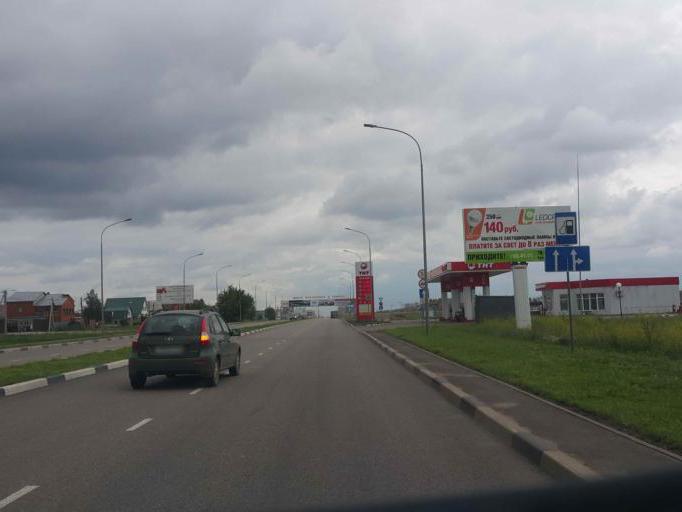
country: RU
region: Tambov
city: Tambov
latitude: 52.7819
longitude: 41.3746
